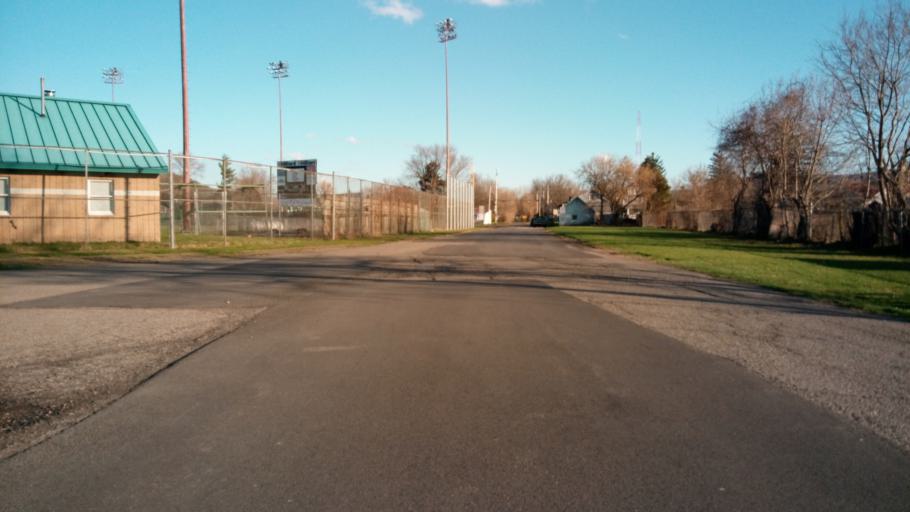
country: US
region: New York
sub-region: Chemung County
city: Elmira
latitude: 42.0803
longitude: -76.7817
